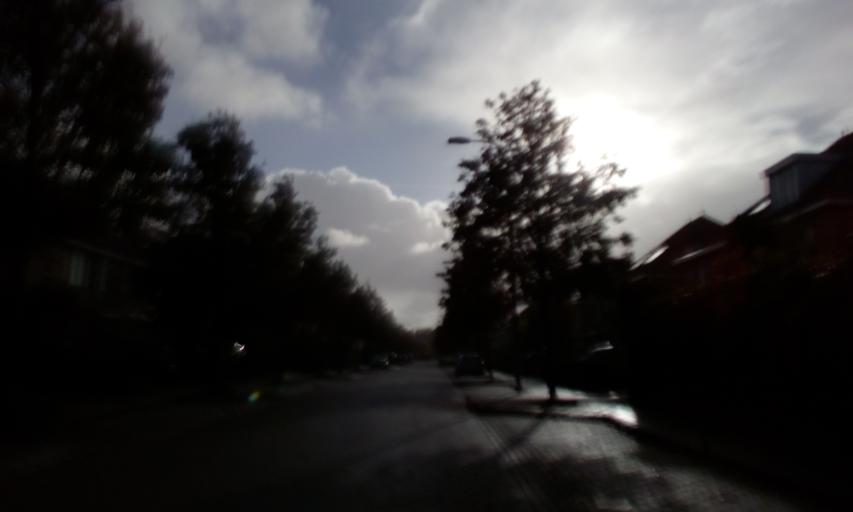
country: NL
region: South Holland
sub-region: Gemeente Lansingerland
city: Berkel en Rodenrijs
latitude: 51.9917
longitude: 4.4673
